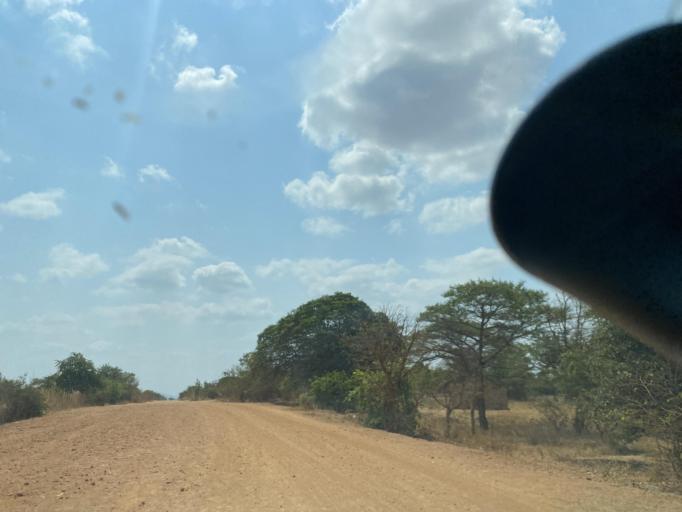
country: ZM
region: Lusaka
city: Chongwe
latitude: -15.5902
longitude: 28.7783
